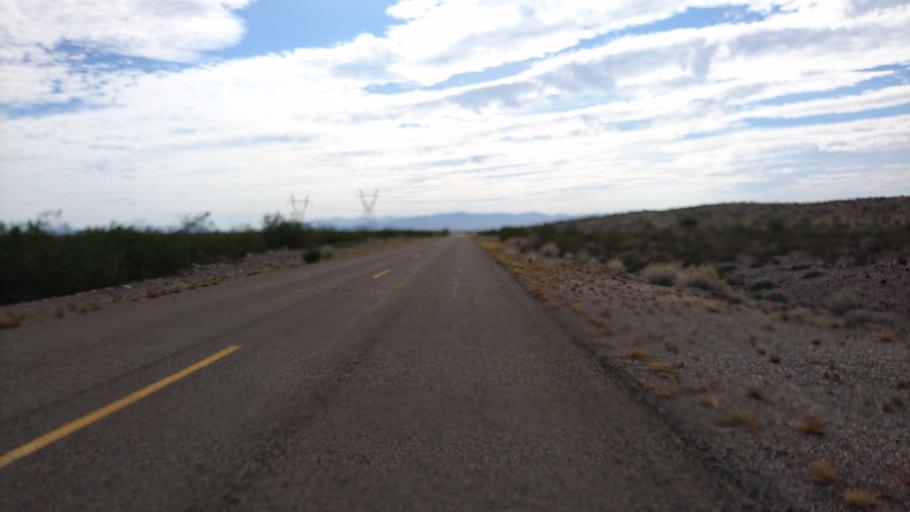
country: US
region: Arizona
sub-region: Mohave County
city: Mohave Valley
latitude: 34.8731
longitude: -114.4383
